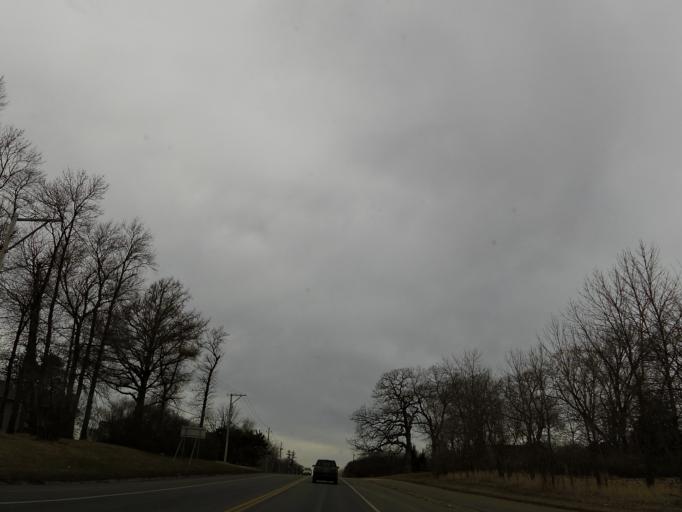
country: US
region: Minnesota
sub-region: Washington County
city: Cottage Grove
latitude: 44.8481
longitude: -92.9242
